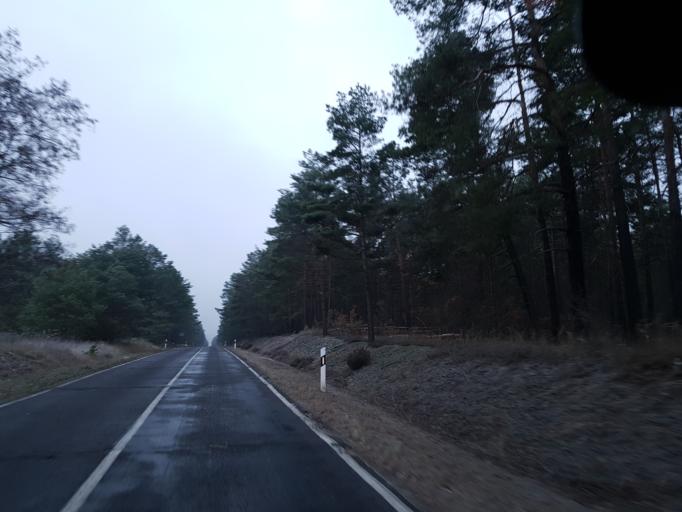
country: DE
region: Brandenburg
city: Schonewalde
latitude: 51.6232
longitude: 13.6392
